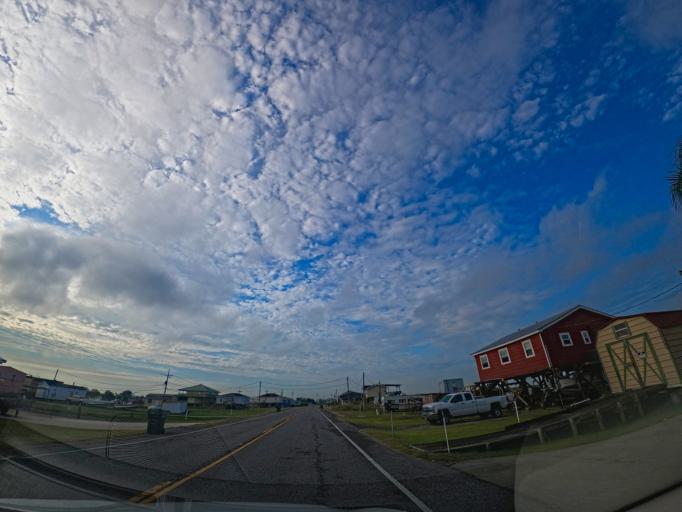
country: US
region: Louisiana
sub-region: Terrebonne Parish
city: Chauvin
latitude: 29.3557
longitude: -90.6262
